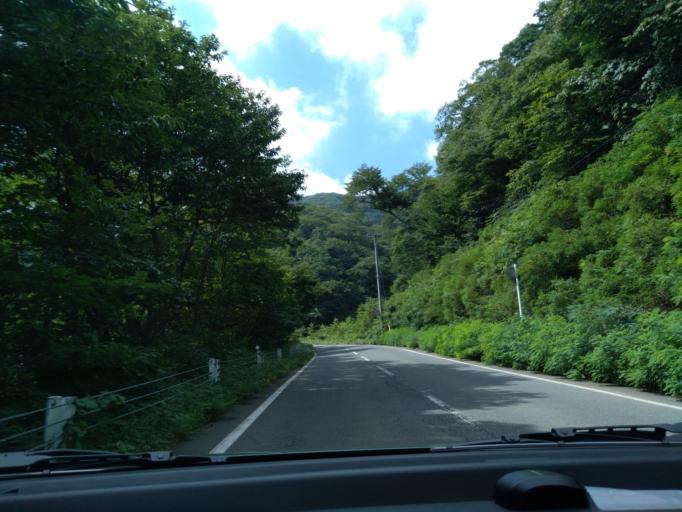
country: JP
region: Iwate
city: Morioka-shi
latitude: 39.6304
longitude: 141.0775
